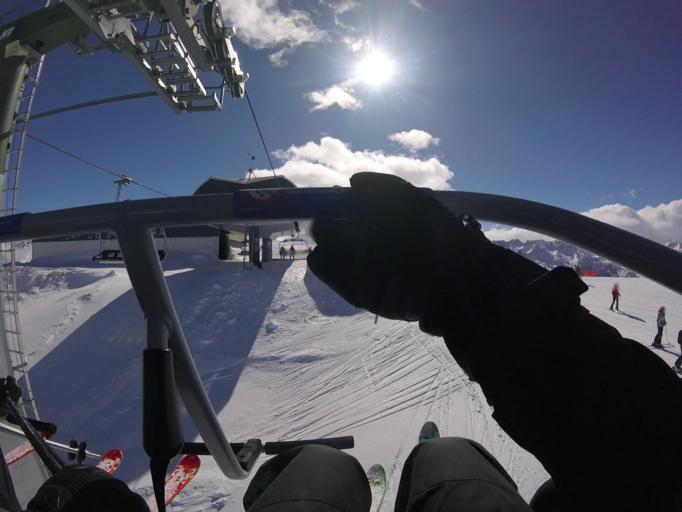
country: ES
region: Catalonia
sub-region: Provincia de Lleida
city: Espot
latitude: 42.6925
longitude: 0.9754
